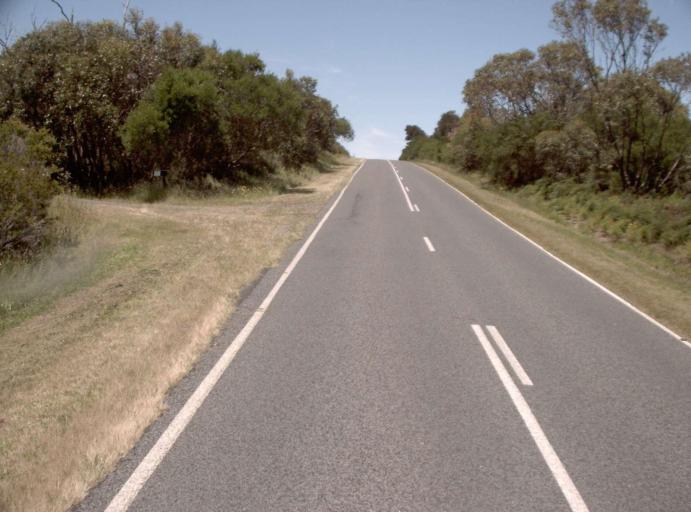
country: AU
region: Victoria
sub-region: Bass Coast
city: North Wonthaggi
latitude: -38.7635
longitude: 146.1525
